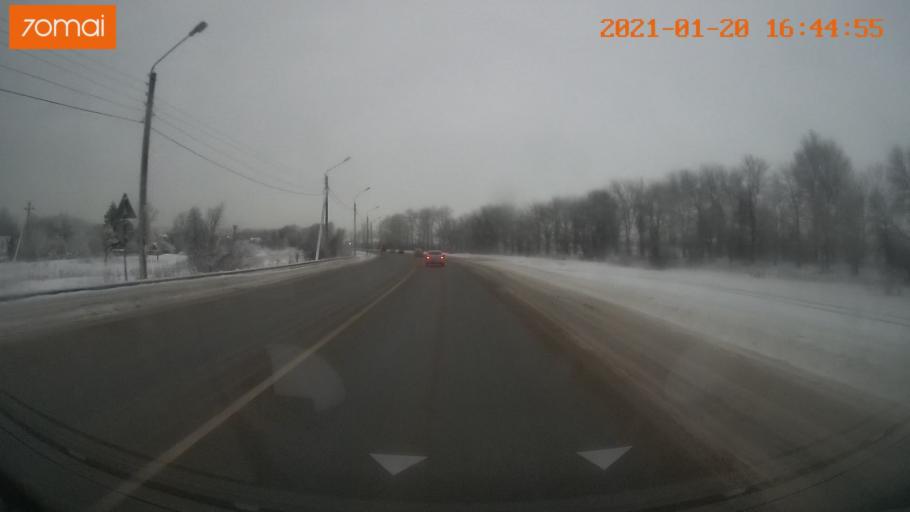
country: RU
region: Vladimir
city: Orgtrud
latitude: 56.2114
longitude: 40.5823
